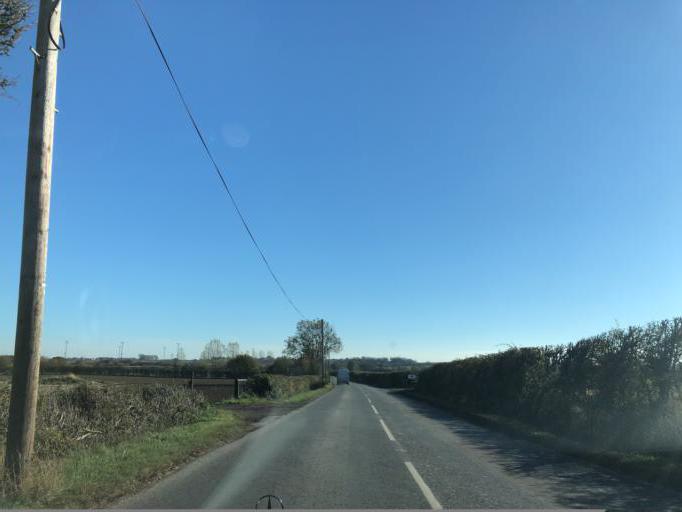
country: GB
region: England
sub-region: Warwickshire
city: Harbury
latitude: 52.2458
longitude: -1.5080
